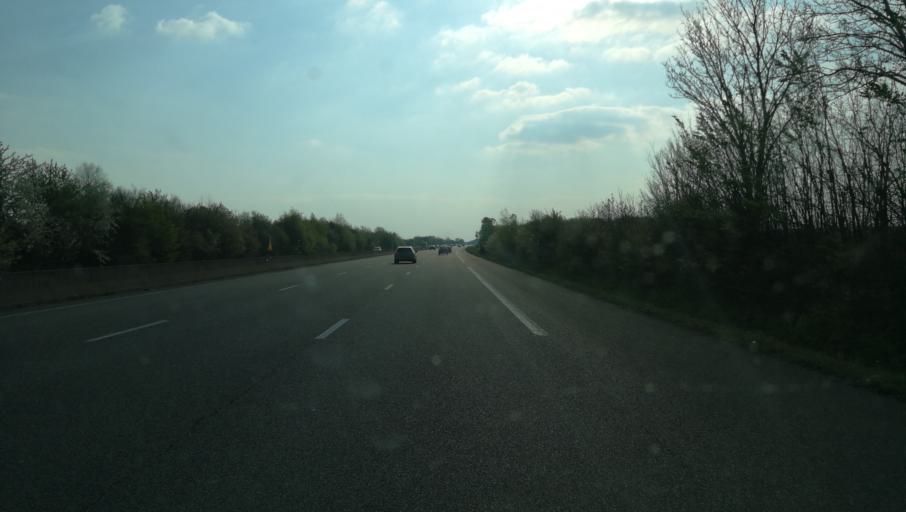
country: FR
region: Ile-de-France
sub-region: Departement des Yvelines
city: Ablis
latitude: 48.5350
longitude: 1.8667
